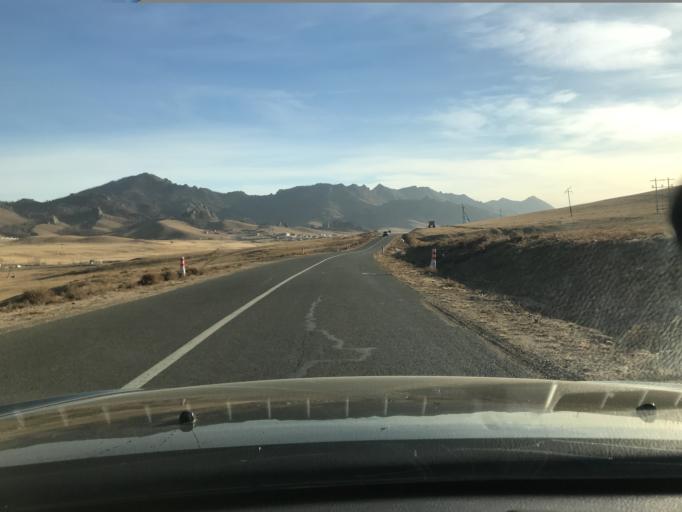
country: MN
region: Central Aimak
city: Arhust
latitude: 47.8795
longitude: 107.4366
